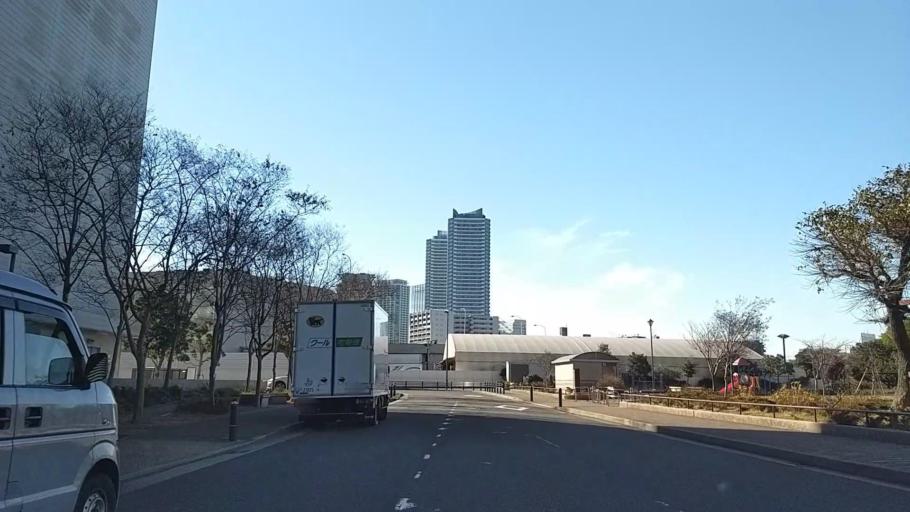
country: JP
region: Kanagawa
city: Yokohama
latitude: 35.4707
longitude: 139.6378
